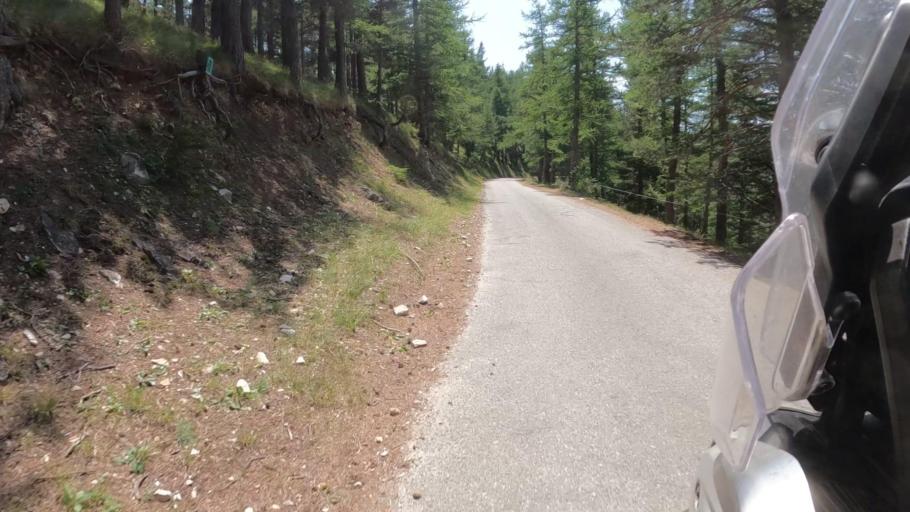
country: IT
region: Piedmont
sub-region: Provincia di Torino
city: Fenestrelle
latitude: 45.0401
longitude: 7.0755
